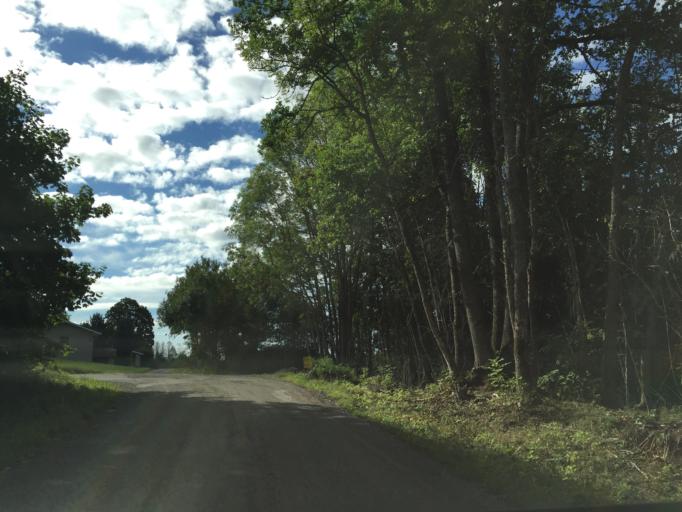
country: NO
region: Vestfold
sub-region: Holmestrand
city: Gullhaug
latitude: 59.4703
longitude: 10.1944
